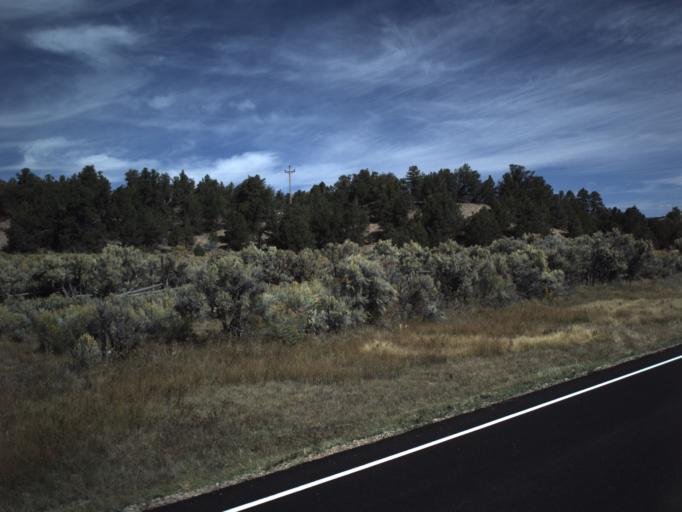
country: US
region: Utah
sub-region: Garfield County
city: Panguitch
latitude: 37.6946
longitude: -111.7959
